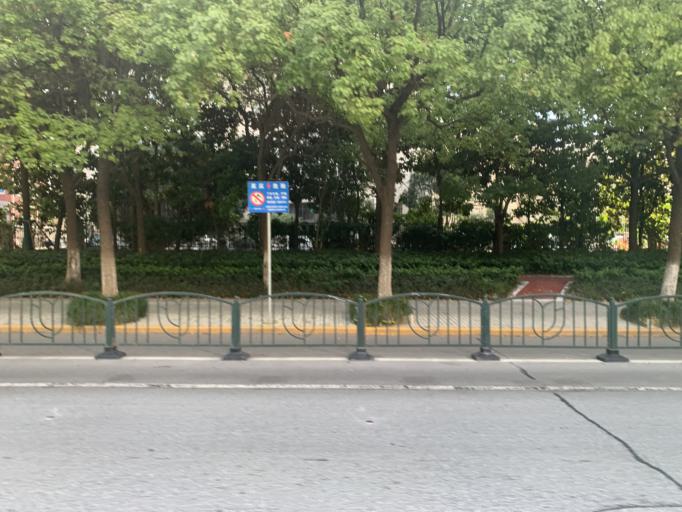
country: CN
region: Shanghai Shi
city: Huamu
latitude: 31.2110
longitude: 121.5277
